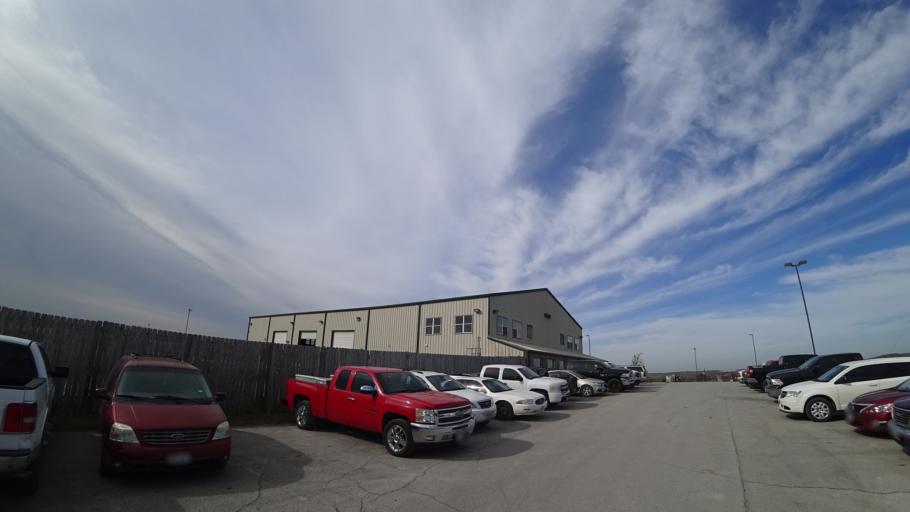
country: US
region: Texas
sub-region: Travis County
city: Onion Creek
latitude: 30.1410
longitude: -97.6903
